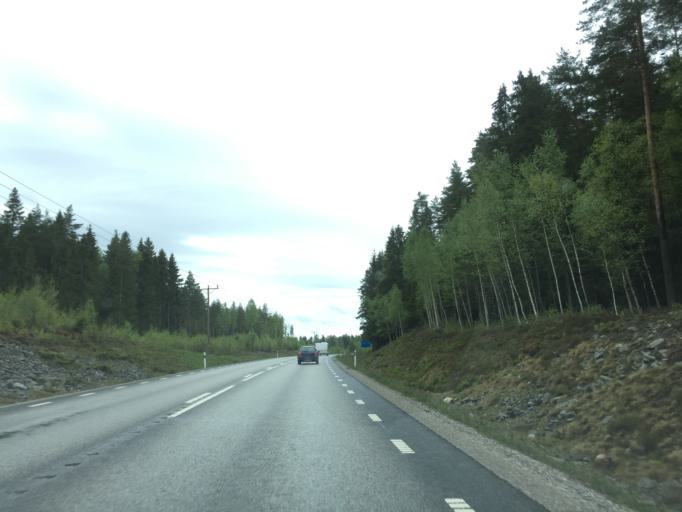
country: SE
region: OErebro
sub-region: Lindesbergs Kommun
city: Lindesberg
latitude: 59.5951
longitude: 15.1841
